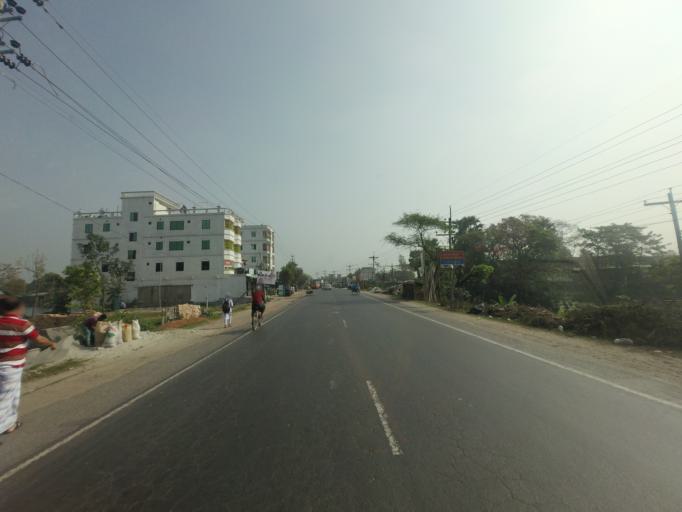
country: BD
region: Dhaka
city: Narsingdi
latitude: 23.8463
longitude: 90.6284
